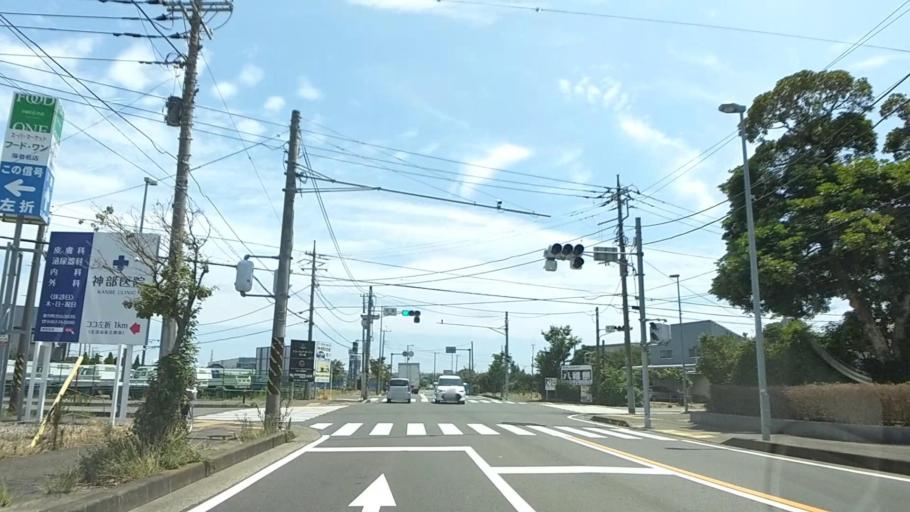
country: JP
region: Kanagawa
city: Chigasaki
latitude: 35.3821
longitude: 139.3841
